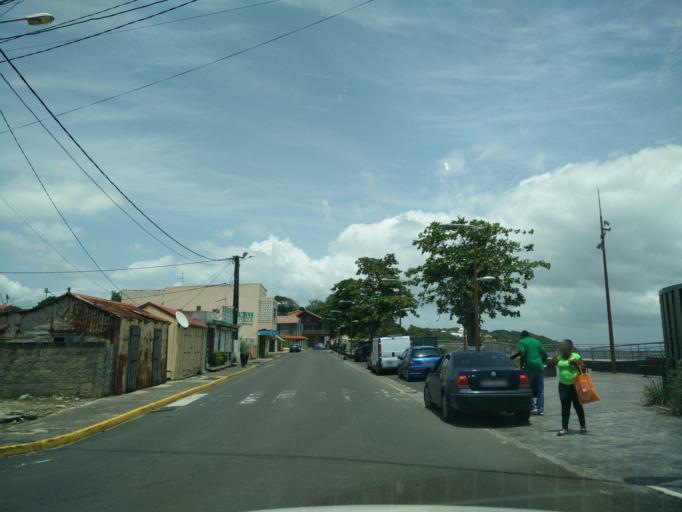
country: GP
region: Guadeloupe
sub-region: Guadeloupe
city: Petit-Bourg
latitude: 16.1921
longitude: -61.5906
